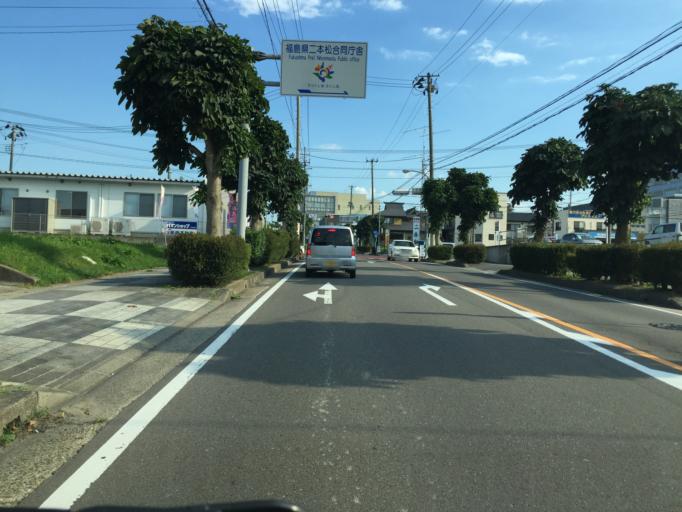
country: JP
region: Fukushima
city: Nihommatsu
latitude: 37.5867
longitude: 140.4324
